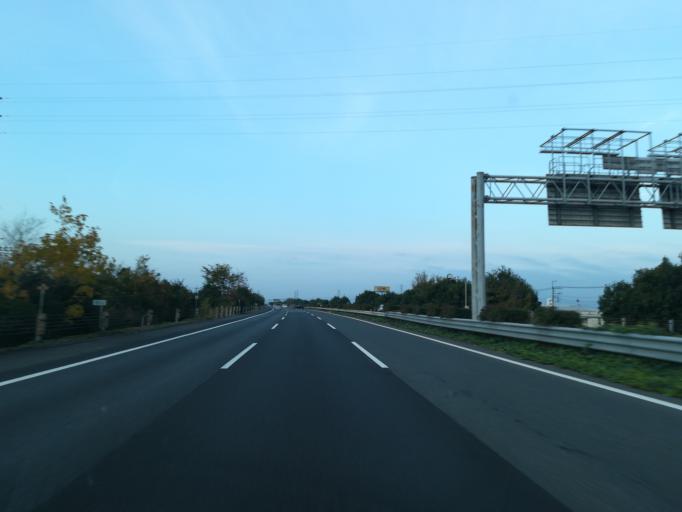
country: JP
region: Gunma
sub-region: Sawa-gun
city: Tamamura
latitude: 36.2917
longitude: 139.0978
